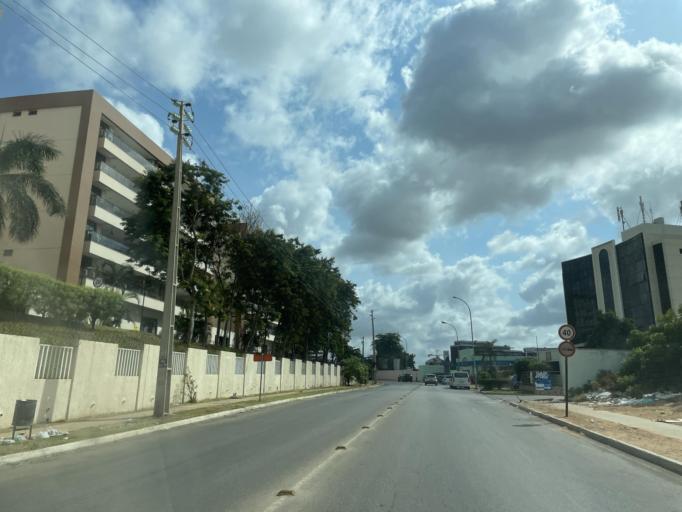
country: AO
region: Luanda
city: Luanda
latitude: -8.9271
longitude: 13.1880
